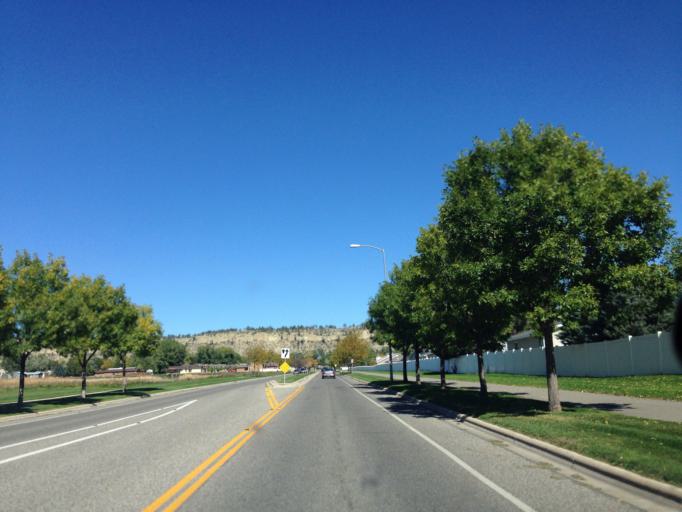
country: US
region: Montana
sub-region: Yellowstone County
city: Billings
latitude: 45.7879
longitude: -108.6007
